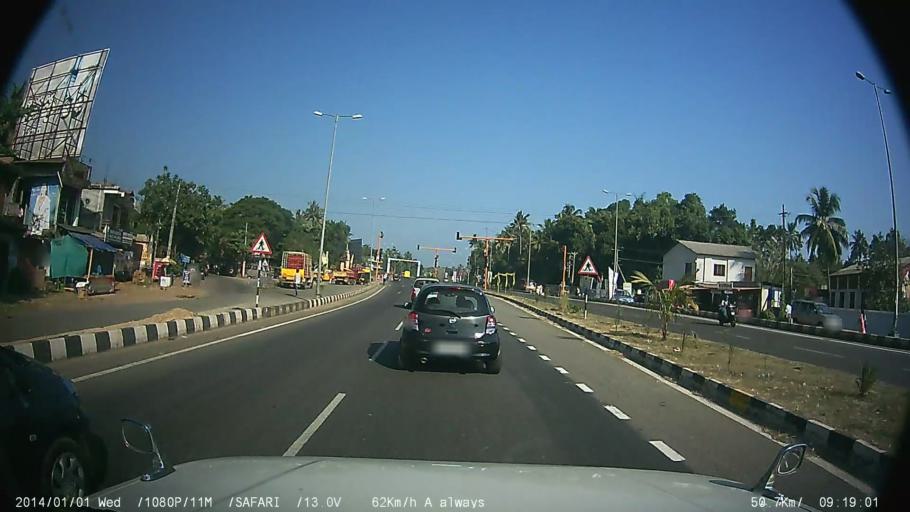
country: IN
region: Kerala
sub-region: Thrissur District
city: Kizhake Chalakudi
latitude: 10.2520
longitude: 76.3678
